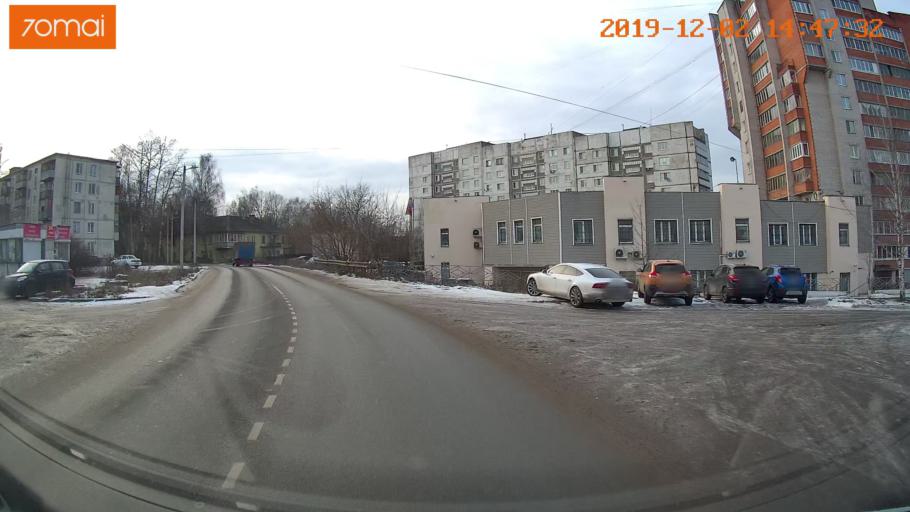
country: RU
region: Ivanovo
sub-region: Gorod Ivanovo
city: Ivanovo
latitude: 56.9886
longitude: 41.0188
